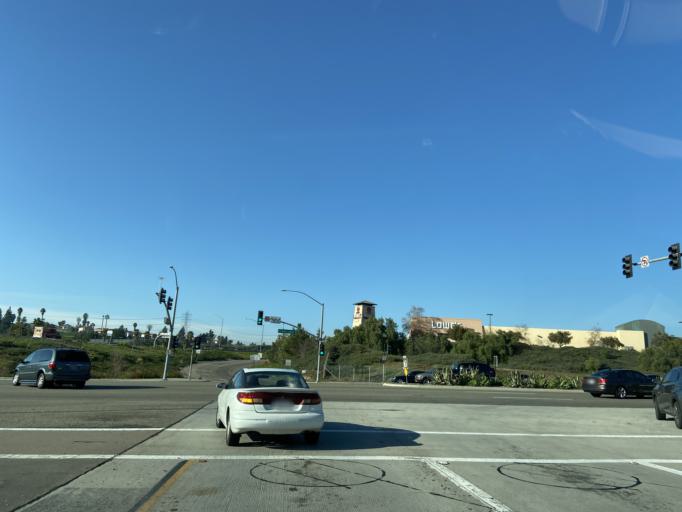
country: US
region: California
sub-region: San Diego County
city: Bonita
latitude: 32.6463
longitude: -116.9695
